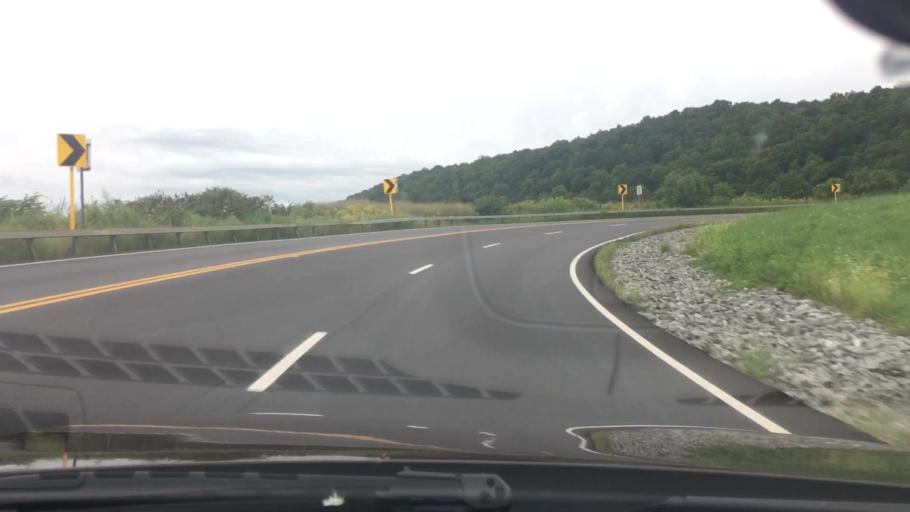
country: US
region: New York
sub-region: Dutchess County
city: Dover Plains
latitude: 41.8377
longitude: -73.5754
